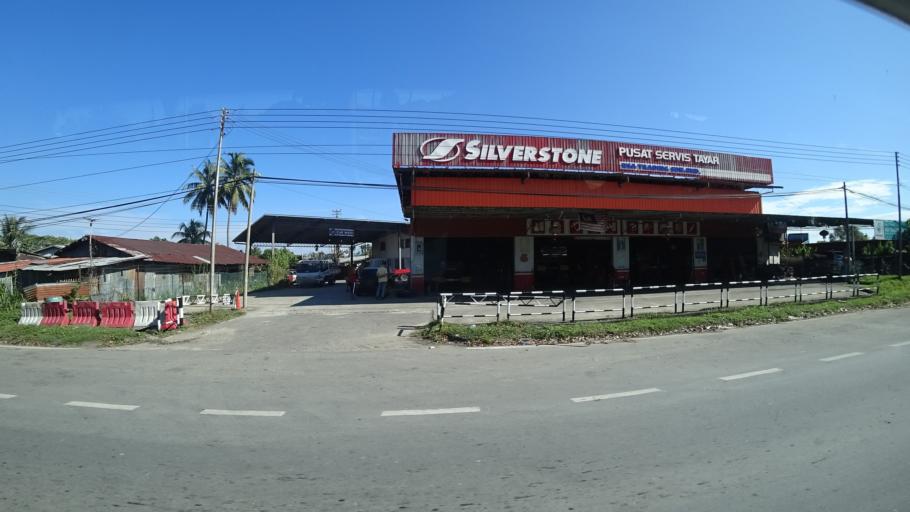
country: MY
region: Sabah
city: Kota Kinabalu
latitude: 6.1471
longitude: 116.2227
